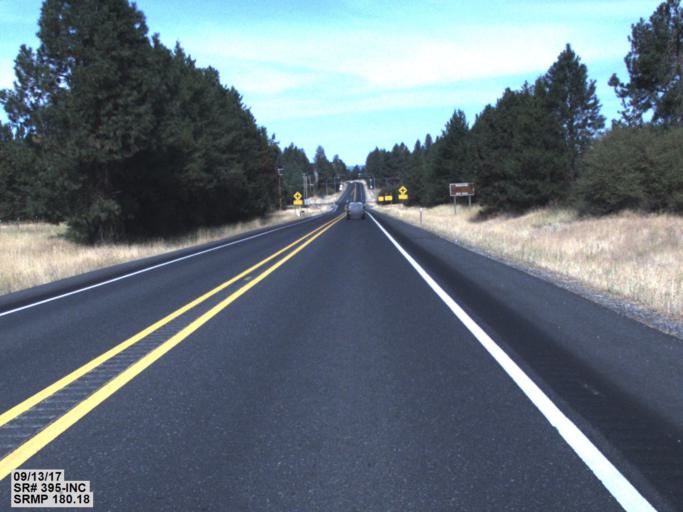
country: US
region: Washington
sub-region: Spokane County
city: Deer Park
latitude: 47.9505
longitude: -117.4849
